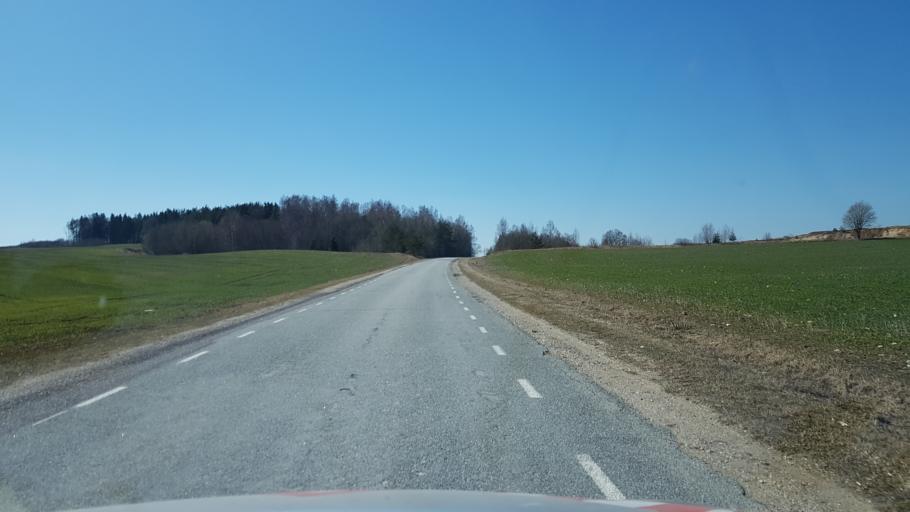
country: EE
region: Laeaene-Virumaa
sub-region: Rakke vald
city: Rakke
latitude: 59.0085
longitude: 26.3312
